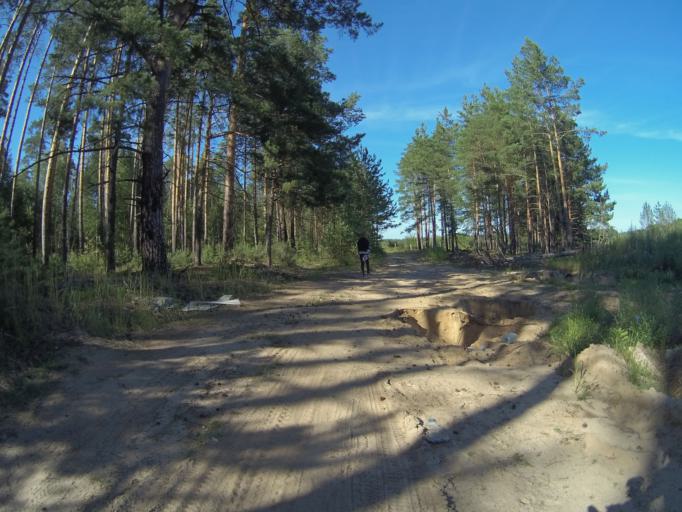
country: RU
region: Vladimir
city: Golovino
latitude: 56.0254
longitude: 40.4166
